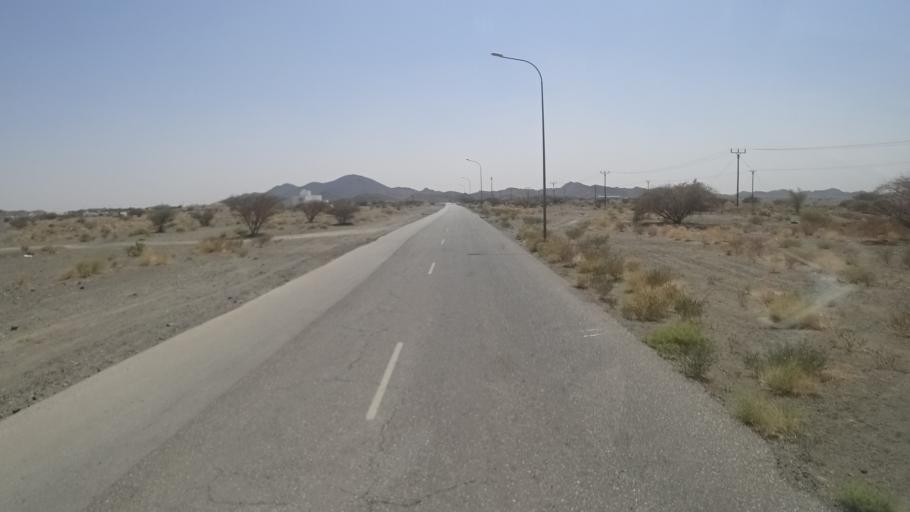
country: OM
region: Ash Sharqiyah
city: Ibra'
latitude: 22.6568
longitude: 58.5257
